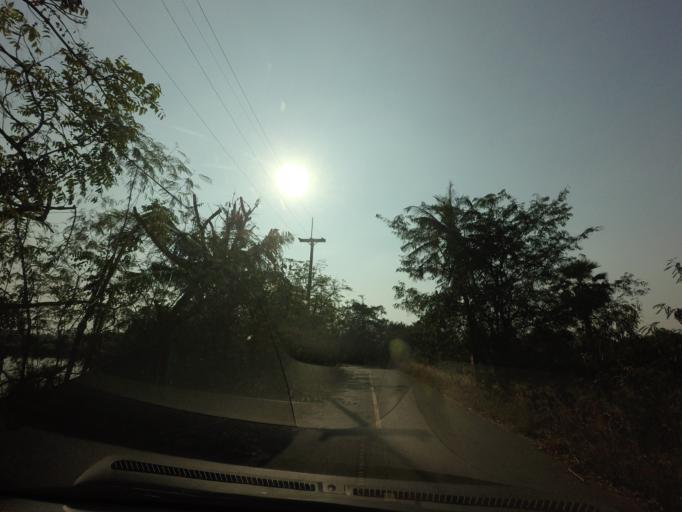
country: TH
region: Chachoengsao
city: Bang Khla
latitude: 13.7563
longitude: 101.1884
